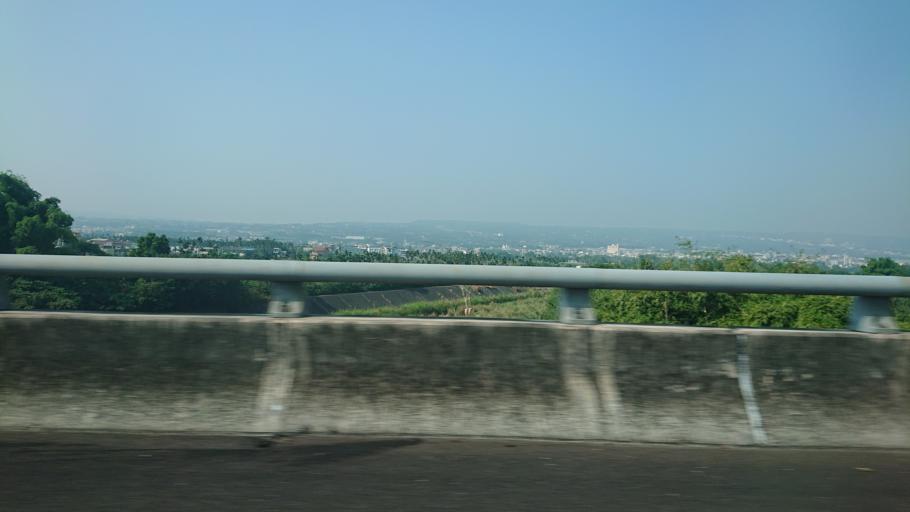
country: TW
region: Taiwan
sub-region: Nantou
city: Nantou
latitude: 23.8947
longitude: 120.7108
